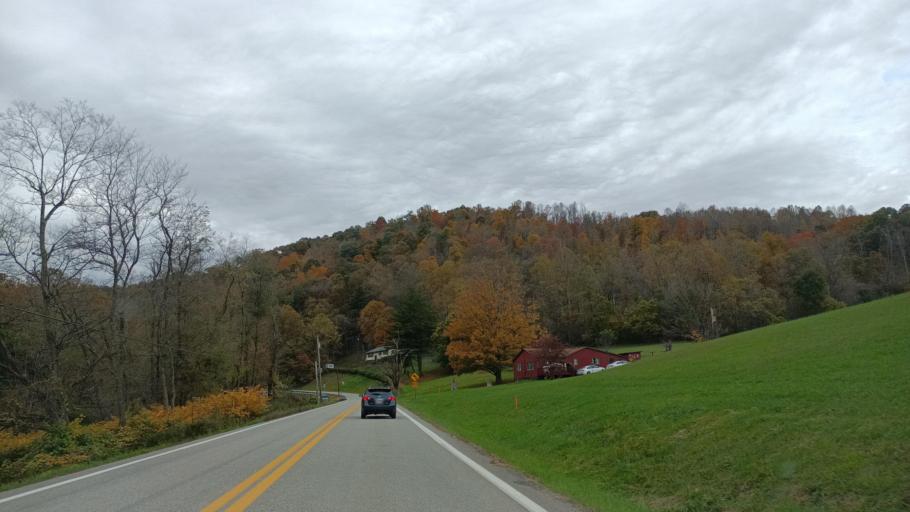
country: US
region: West Virginia
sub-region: Taylor County
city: Grafton
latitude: 39.3443
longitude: -79.9505
